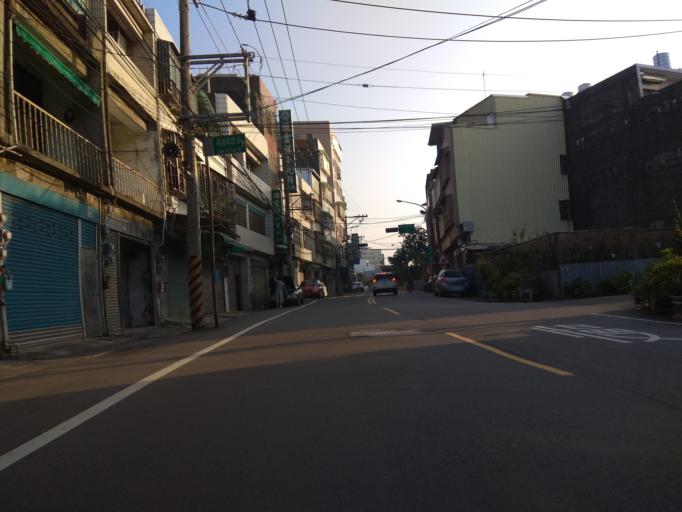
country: TW
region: Taiwan
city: Daxi
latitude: 24.9181
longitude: 121.1864
